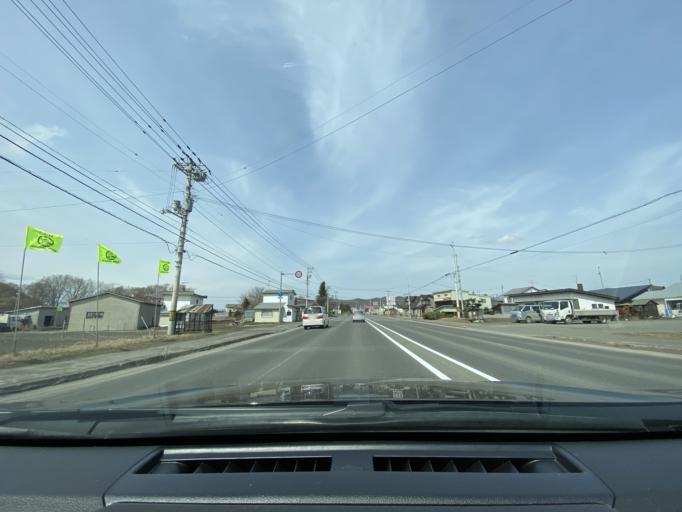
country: JP
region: Hokkaido
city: Kitami
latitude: 43.8028
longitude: 143.8159
